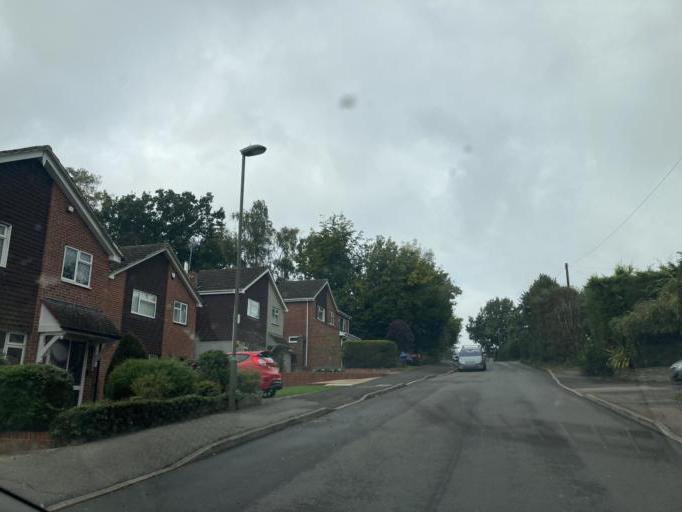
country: GB
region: England
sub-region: Surrey
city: Bagshot
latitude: 51.3590
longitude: -0.6990
